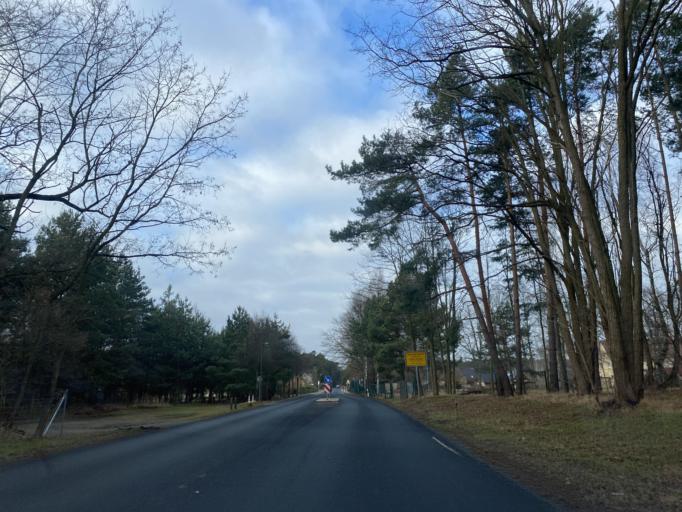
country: PL
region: Lubusz
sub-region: Powiat zarski
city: Leknica
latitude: 51.4998
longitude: 14.8146
